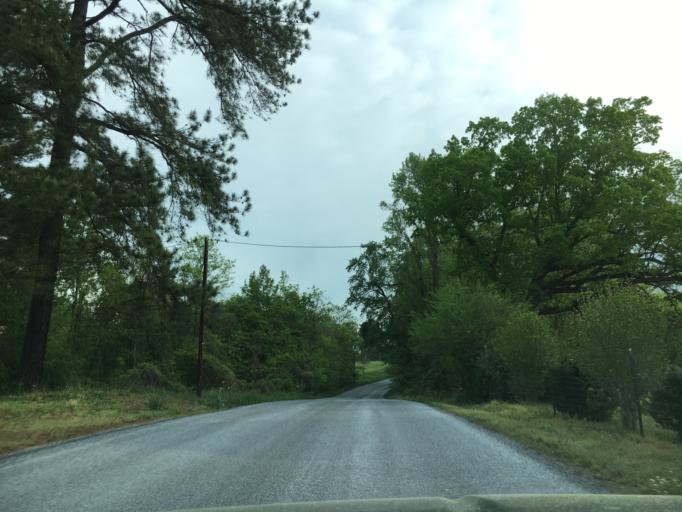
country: US
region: Virginia
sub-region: Campbell County
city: Brookneal
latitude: 36.9356
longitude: -78.9473
